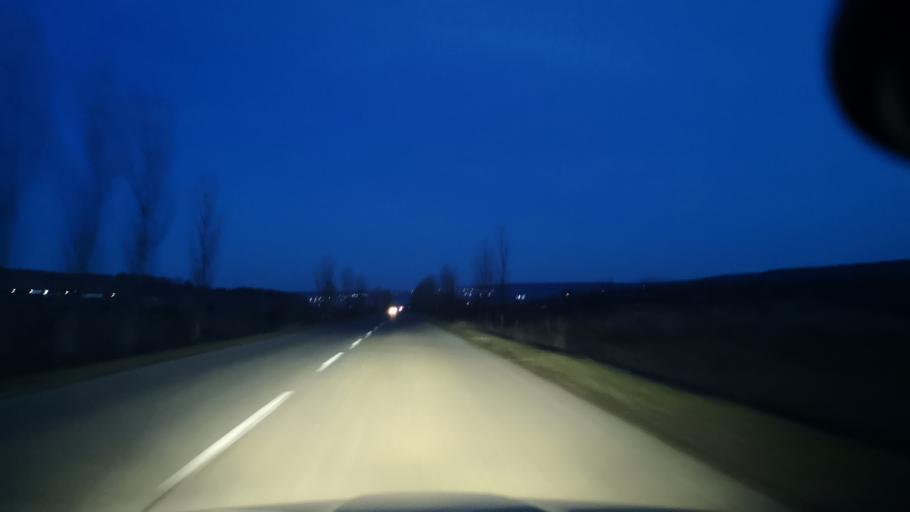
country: MD
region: Orhei
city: Orhei
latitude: 47.3441
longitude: 28.7373
